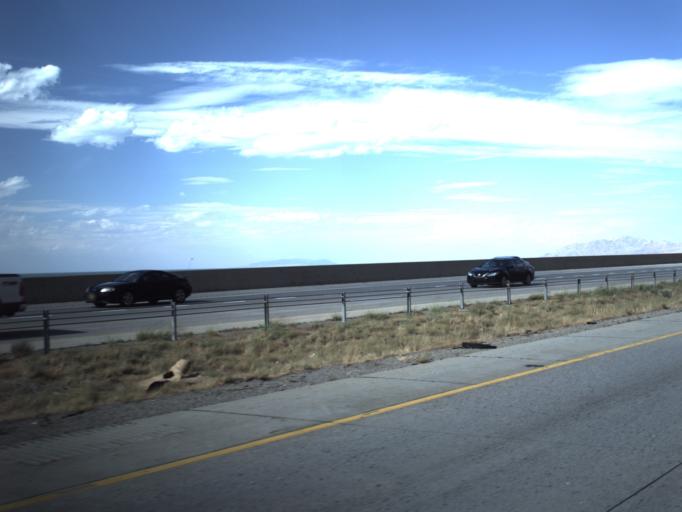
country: US
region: Utah
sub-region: Tooele County
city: Stansbury park
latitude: 40.7043
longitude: -112.2558
